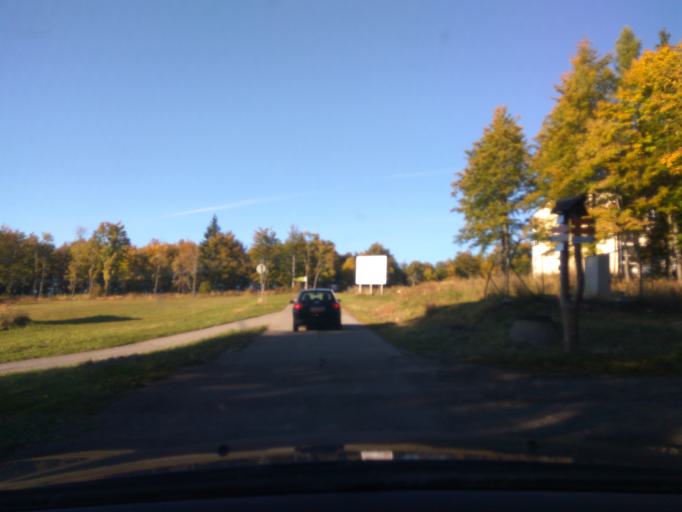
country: SK
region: Banskobystricky
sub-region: Okres Ziar nad Hronom
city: Kremnica
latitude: 48.7387
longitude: 18.9888
